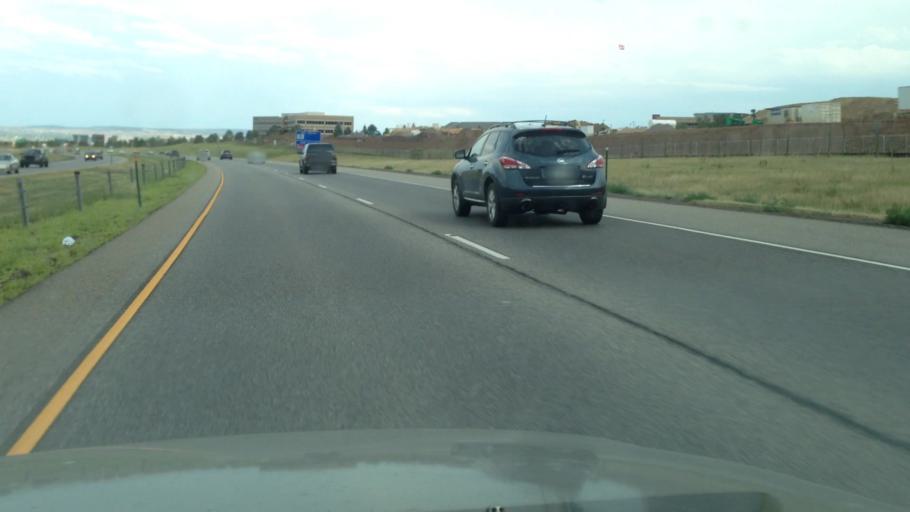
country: US
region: Colorado
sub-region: Jefferson County
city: Ken Caryl
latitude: 39.5622
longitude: -105.1242
